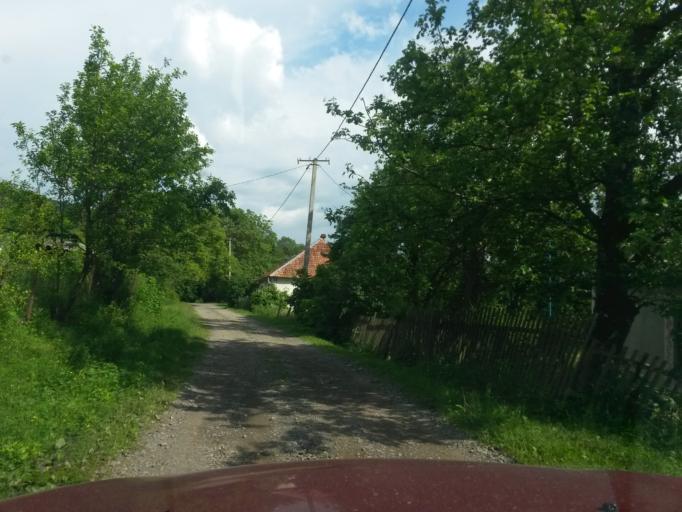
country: UA
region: Zakarpattia
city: Velykyi Bereznyi
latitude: 48.9017
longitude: 22.5247
